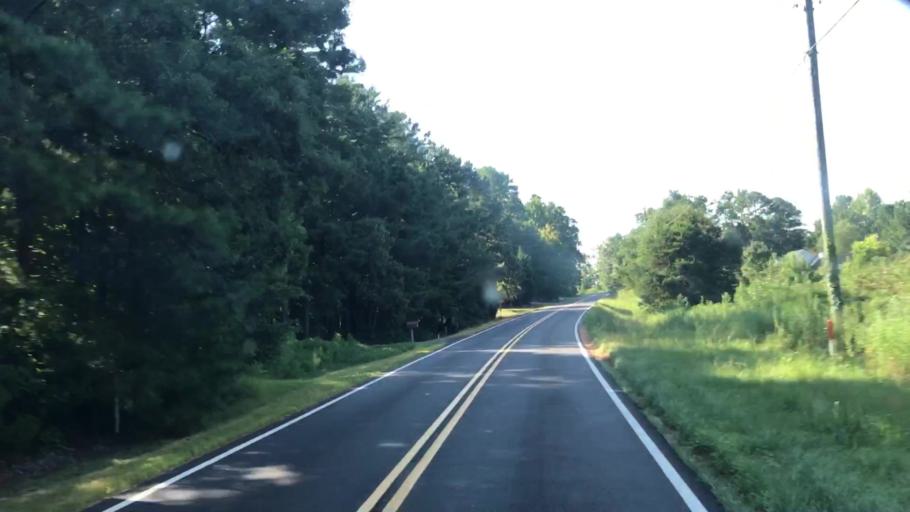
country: US
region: Georgia
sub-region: Walton County
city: Loganville
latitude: 33.8723
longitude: -83.8018
